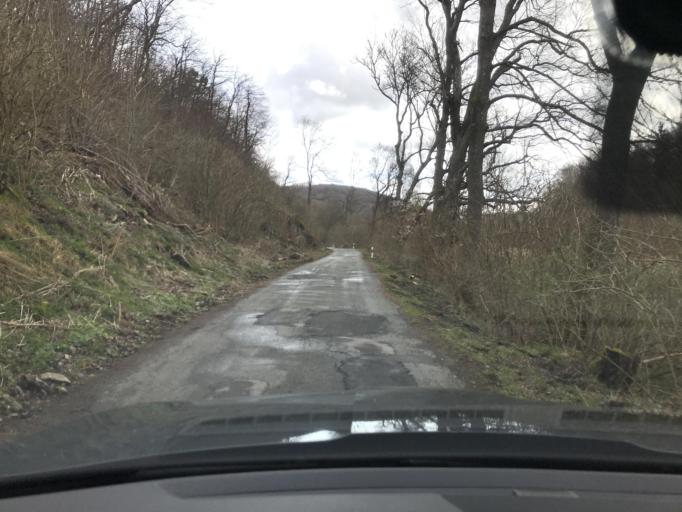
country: DE
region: Saxony-Anhalt
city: Harzgerode
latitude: 51.6757
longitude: 11.1773
